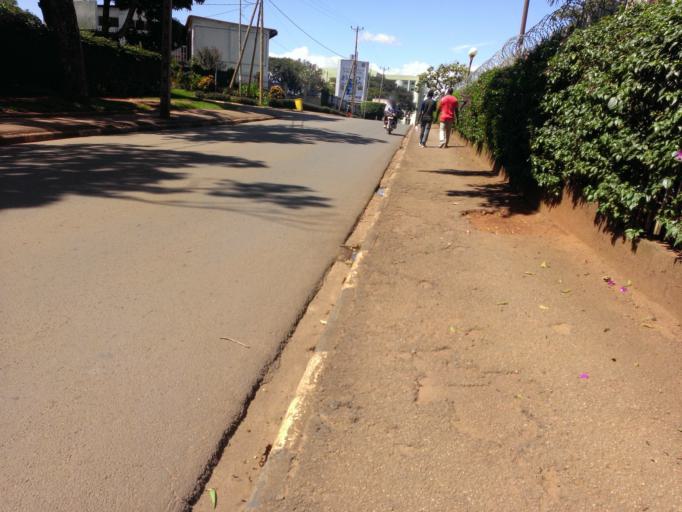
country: UG
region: Central Region
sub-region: Kampala District
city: Kampala
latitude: 0.3171
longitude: 32.5827
